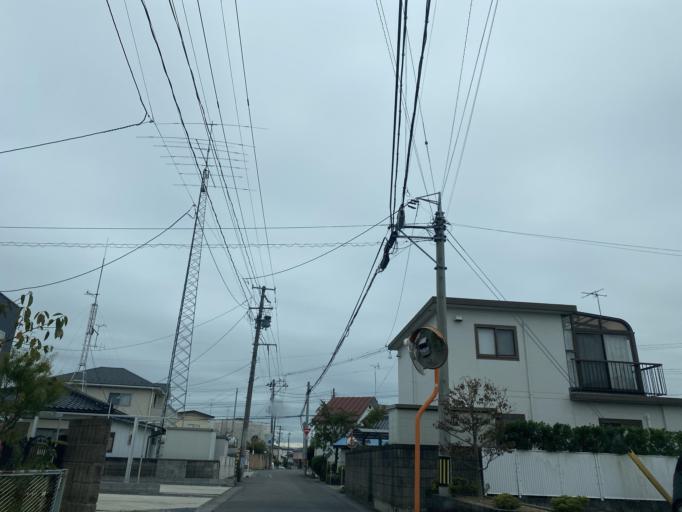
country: JP
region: Fukushima
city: Koriyama
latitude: 37.3785
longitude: 140.3332
